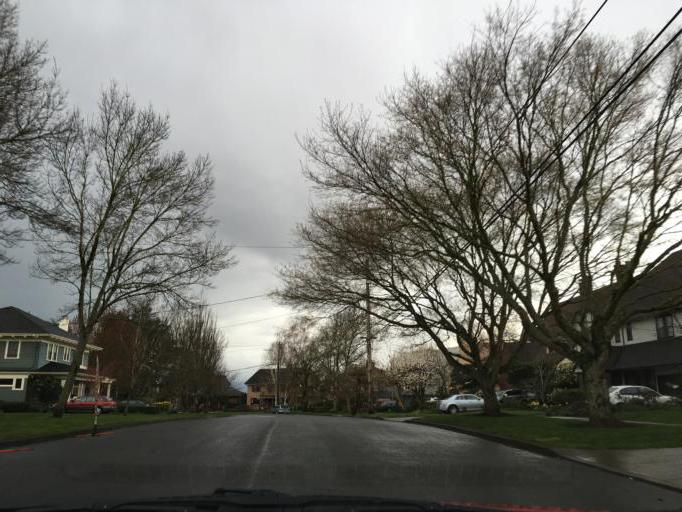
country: US
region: Oregon
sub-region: Multnomah County
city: Portland
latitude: 45.5464
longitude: -122.6239
